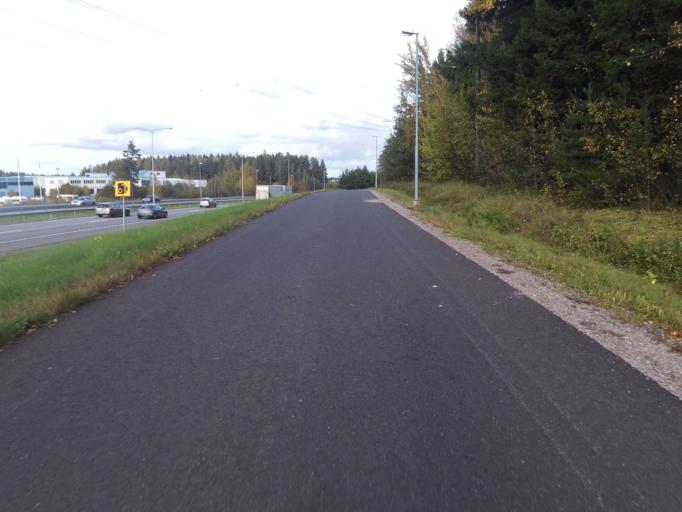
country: FI
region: Uusimaa
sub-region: Helsinki
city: Kauniainen
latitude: 60.2595
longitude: 24.7241
